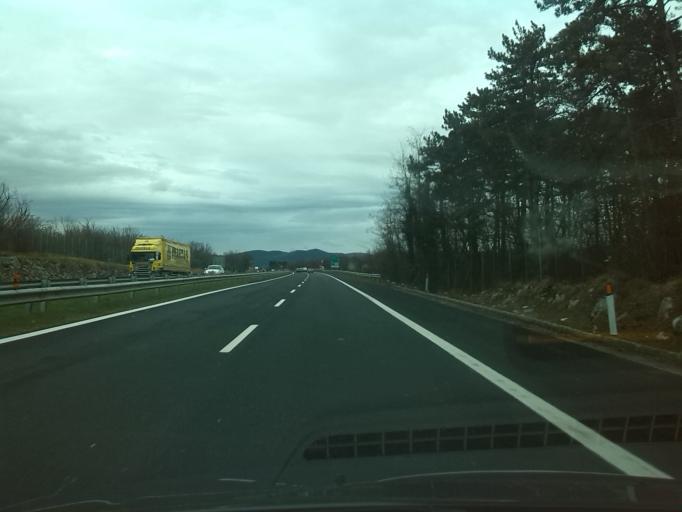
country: IT
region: Friuli Venezia Giulia
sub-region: Provincia di Trieste
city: Villa Opicina
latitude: 45.6783
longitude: 13.8175
